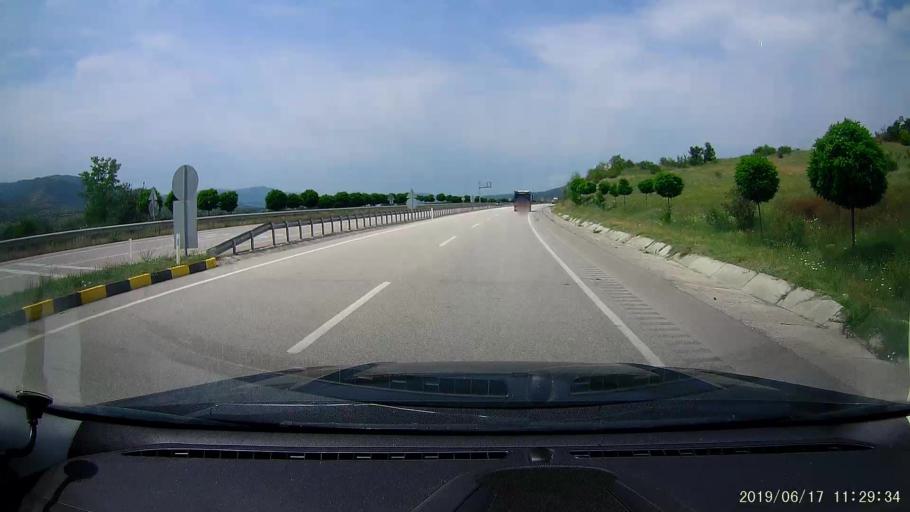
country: TR
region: Cankiri
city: Ilgaz
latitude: 40.9079
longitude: 33.5952
